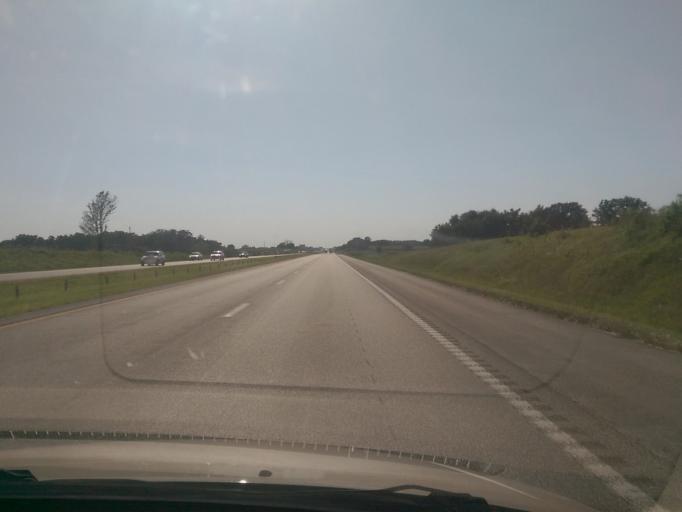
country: US
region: Missouri
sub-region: Saline County
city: Sweet Springs
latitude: 38.9720
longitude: -93.2834
